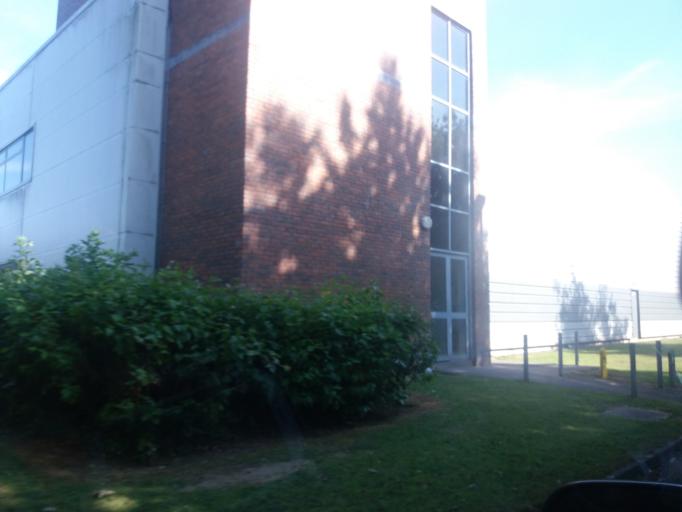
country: IE
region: Leinster
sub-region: Fingal County
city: Blanchardstown
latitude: 53.4022
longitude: -6.3660
